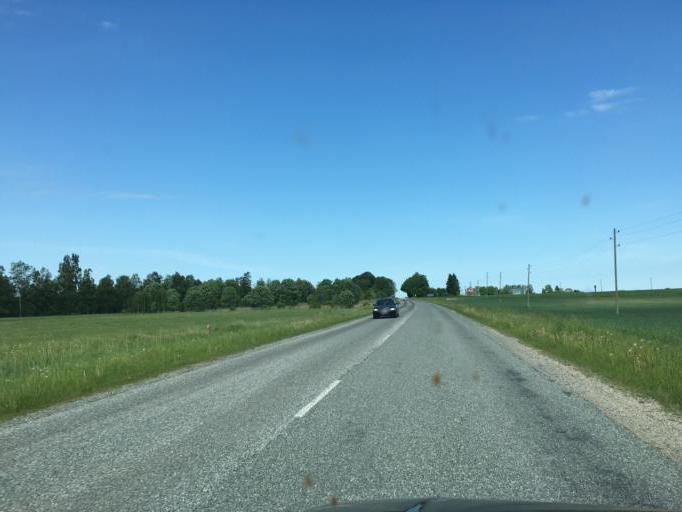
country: LV
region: Talsu Rajons
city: Valdemarpils
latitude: 57.3707
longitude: 22.4835
